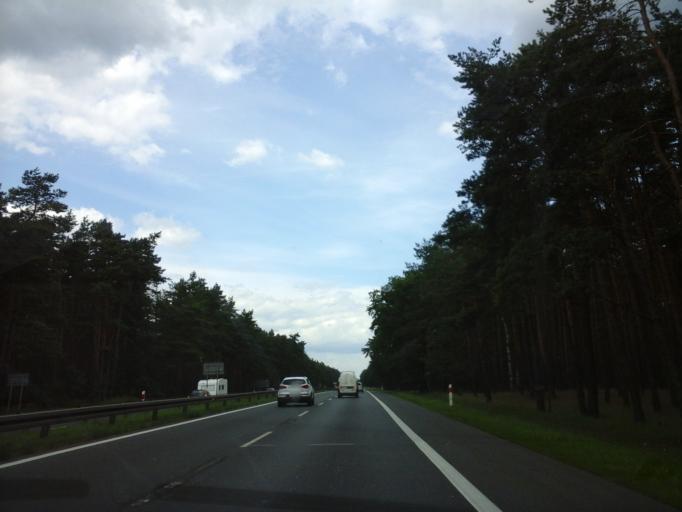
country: PL
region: West Pomeranian Voivodeship
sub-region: Powiat stargardzki
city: Kobylanka
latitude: 53.4285
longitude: 14.7725
